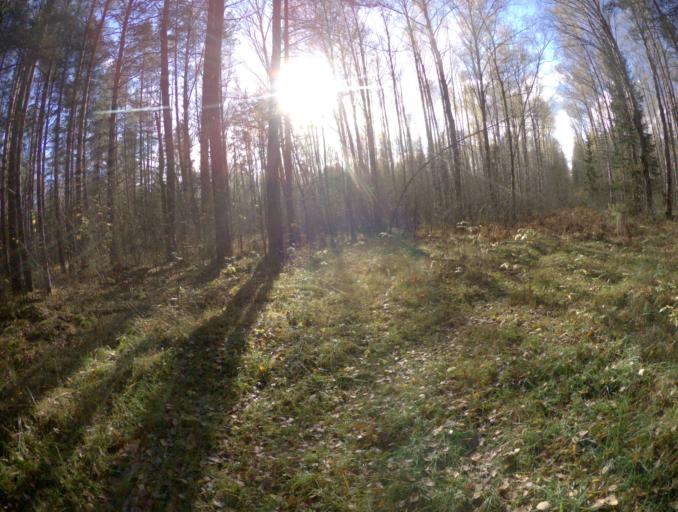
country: RU
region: Vladimir
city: Raduzhnyy
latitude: 56.0589
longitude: 40.3434
